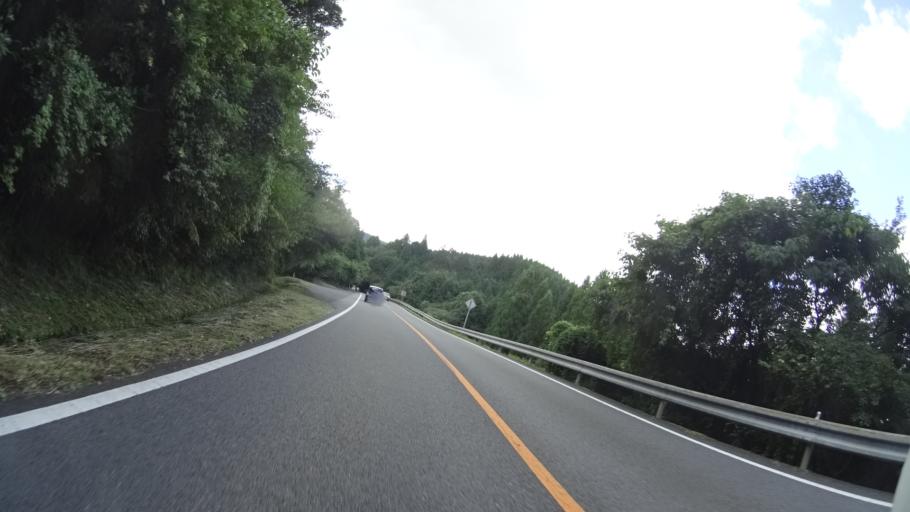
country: JP
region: Oita
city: Tsukawaki
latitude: 33.2366
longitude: 131.2867
